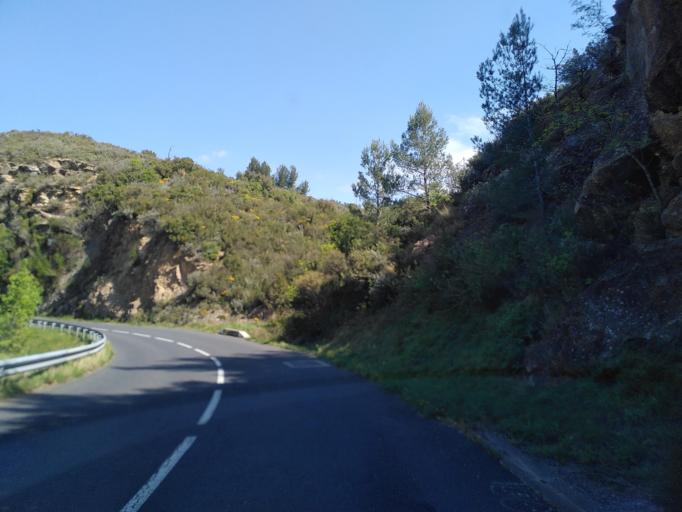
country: FR
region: Languedoc-Roussillon
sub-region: Departement de l'Aude
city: Portel-des-Corbieres
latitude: 42.9894
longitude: 2.7899
